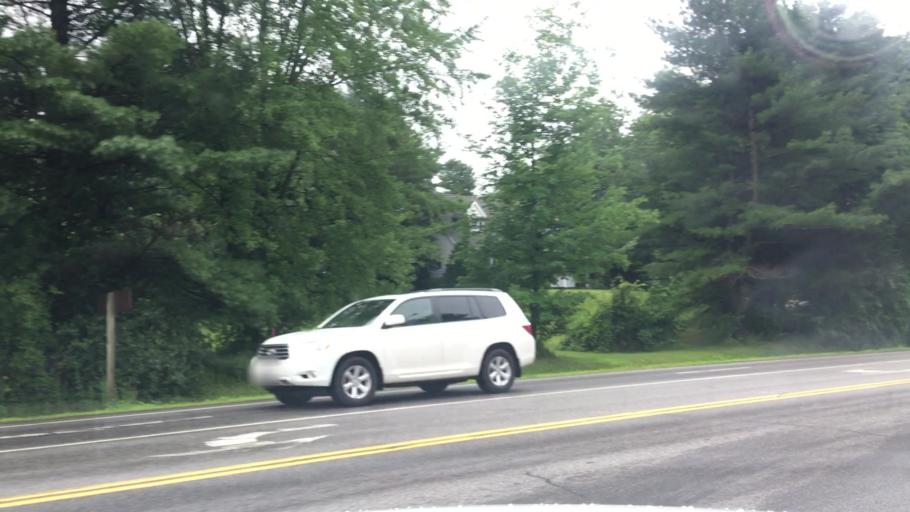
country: US
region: Maine
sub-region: Kennebec County
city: Augusta
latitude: 44.3559
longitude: -69.7972
